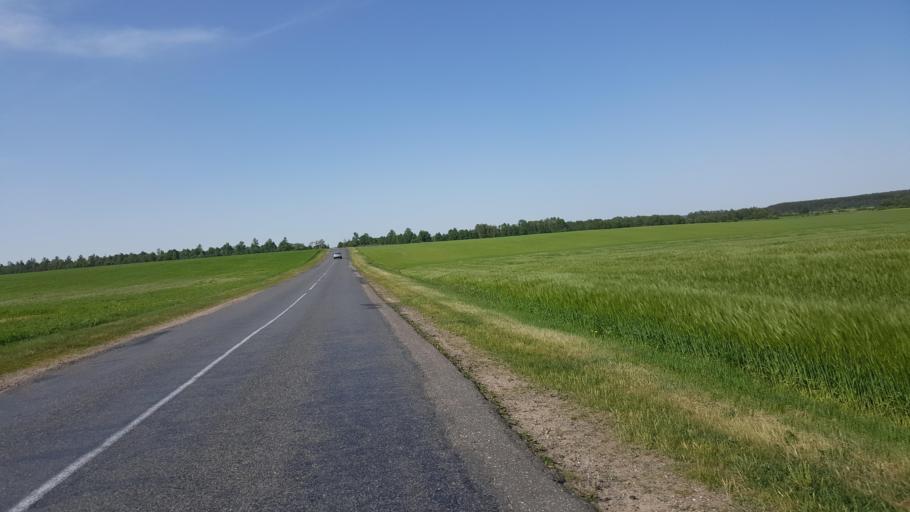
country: BY
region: Brest
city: Charnawchytsy
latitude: 52.3029
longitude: 23.6070
